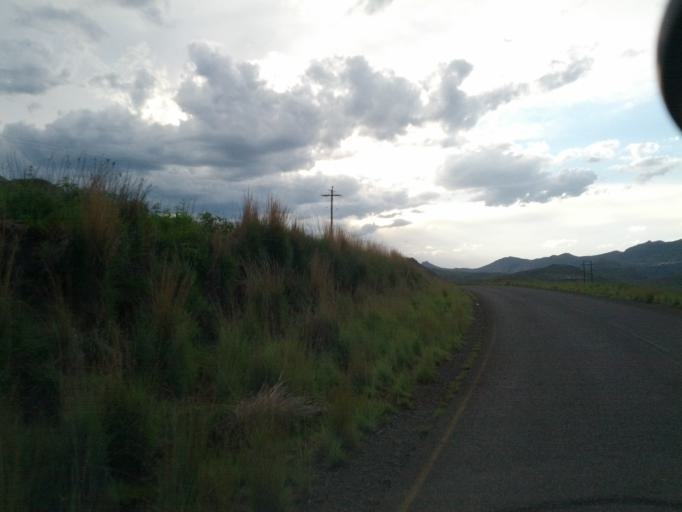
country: LS
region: Qacha's Nek
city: Qacha's Nek
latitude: -30.0669
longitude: 28.5536
